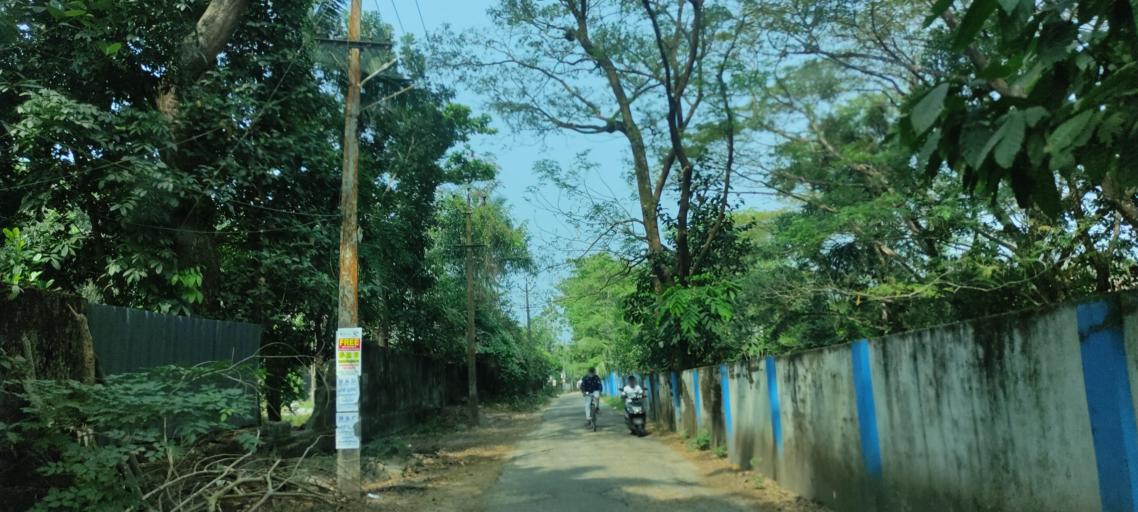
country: IN
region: Kerala
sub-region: Alappuzha
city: Shertallai
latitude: 9.6821
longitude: 76.3378
